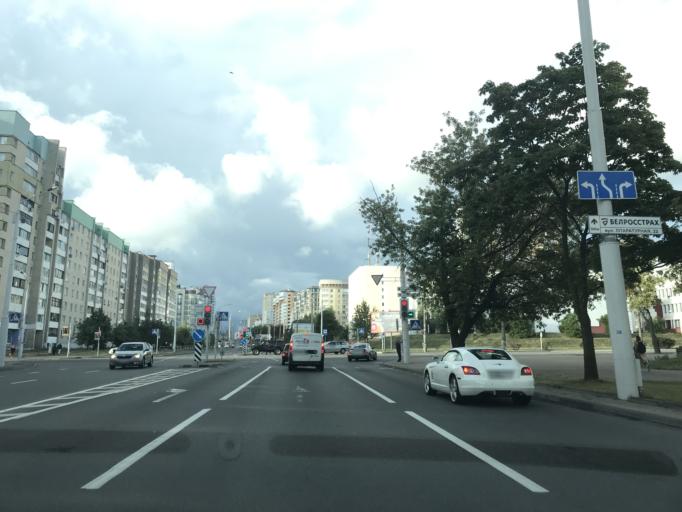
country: BY
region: Minsk
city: Minsk
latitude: 53.9324
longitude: 27.5896
